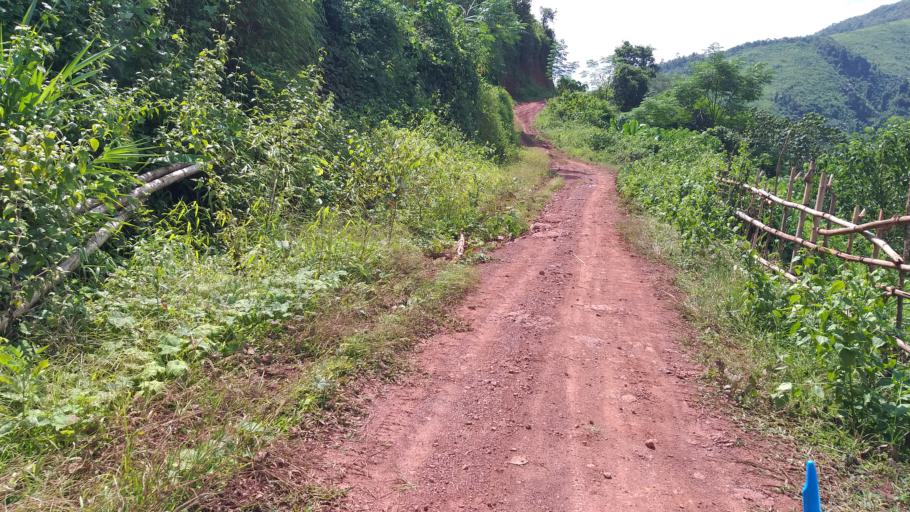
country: LA
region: Phongsali
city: Khoa
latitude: 21.2925
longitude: 102.5429
